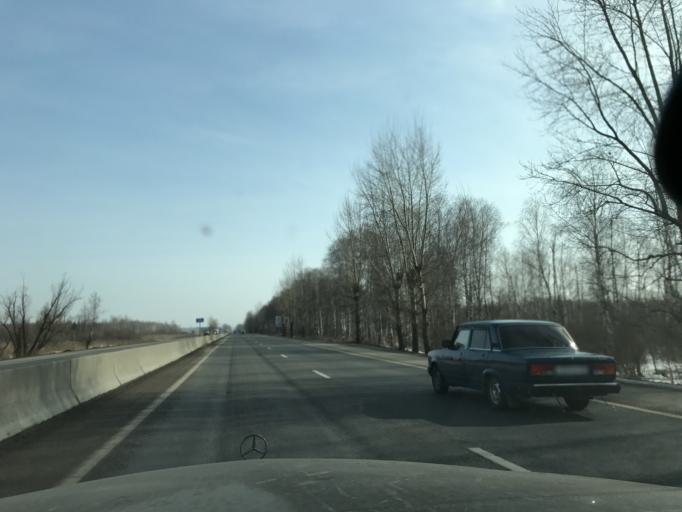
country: RU
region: Nizjnij Novgorod
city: Gorbatovka
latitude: 56.3099
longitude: 43.7741
